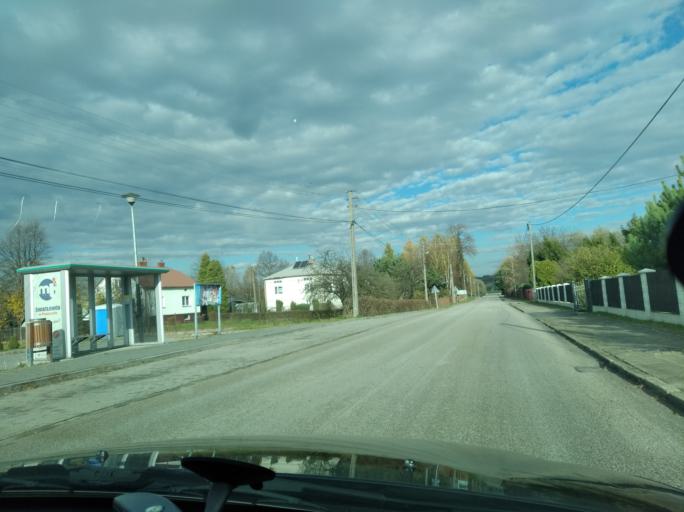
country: PL
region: Subcarpathian Voivodeship
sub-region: Powiat debicki
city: Brzeznica
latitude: 50.0875
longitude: 21.5210
